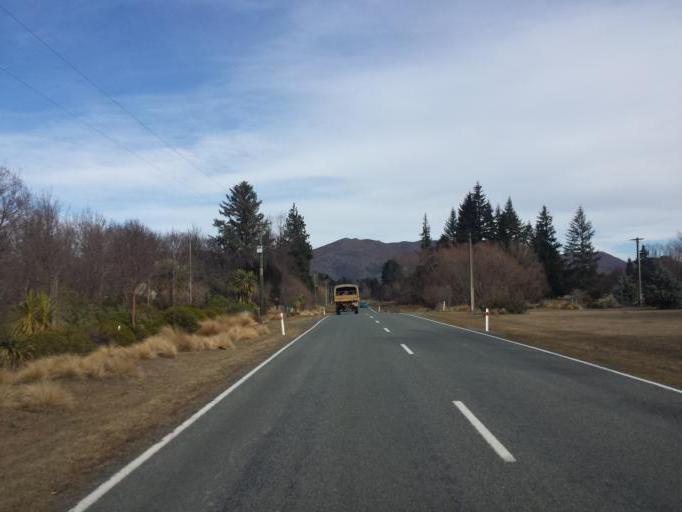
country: NZ
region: Canterbury
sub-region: Timaru District
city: Pleasant Point
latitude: -44.0834
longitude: 170.6596
